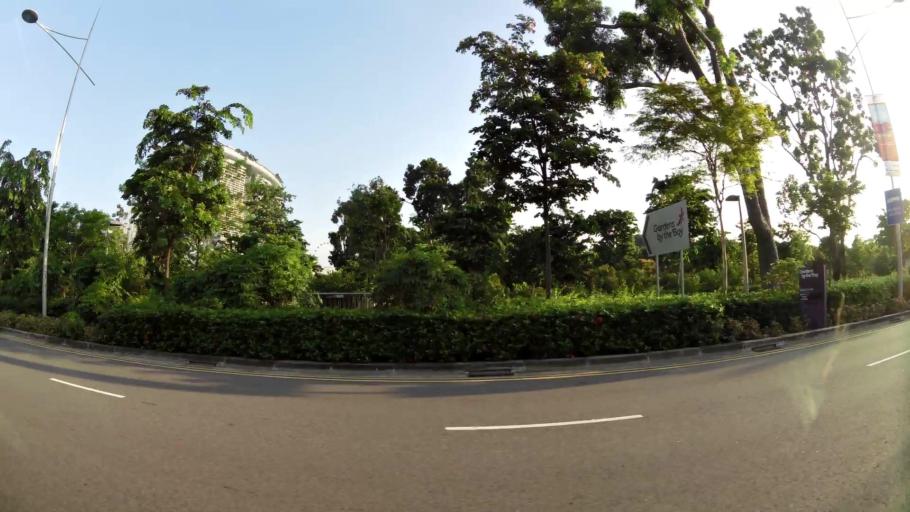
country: SG
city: Singapore
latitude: 1.2770
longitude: 103.8601
